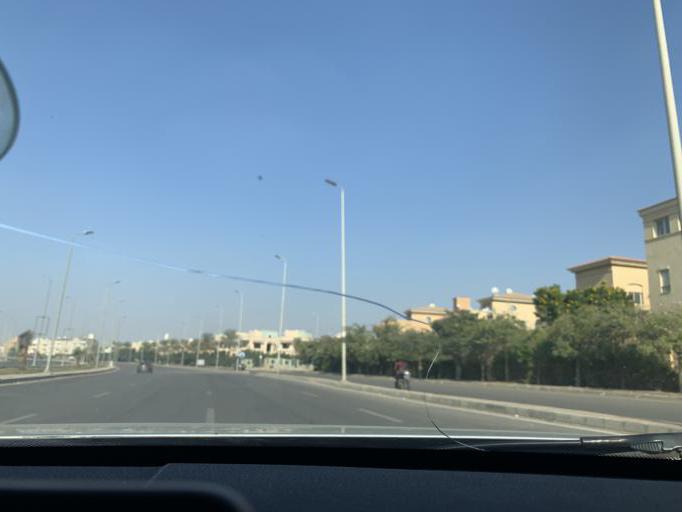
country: EG
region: Muhafazat al Qalyubiyah
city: Al Khankah
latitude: 30.0104
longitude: 31.4740
